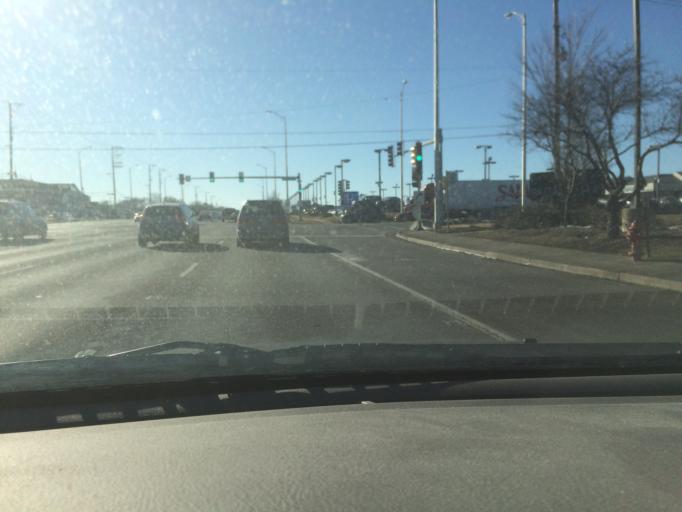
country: US
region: Illinois
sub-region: Cook County
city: Hoffman Estates
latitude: 42.0501
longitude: -88.0592
